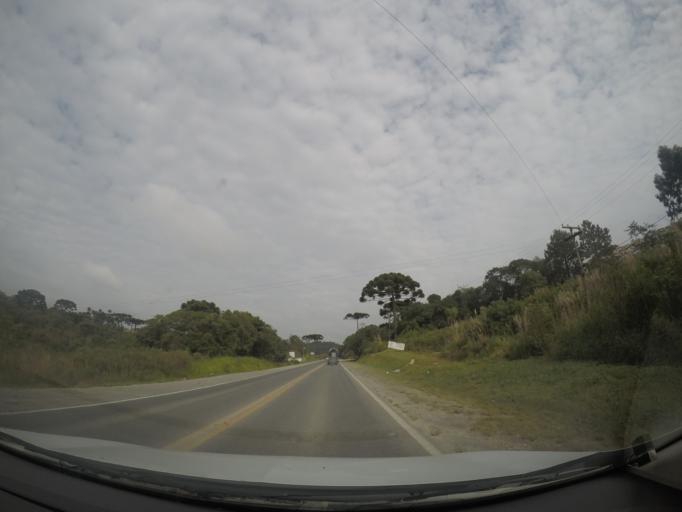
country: BR
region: Parana
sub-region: Almirante Tamandare
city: Almirante Tamandare
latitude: -25.3386
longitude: -49.2581
